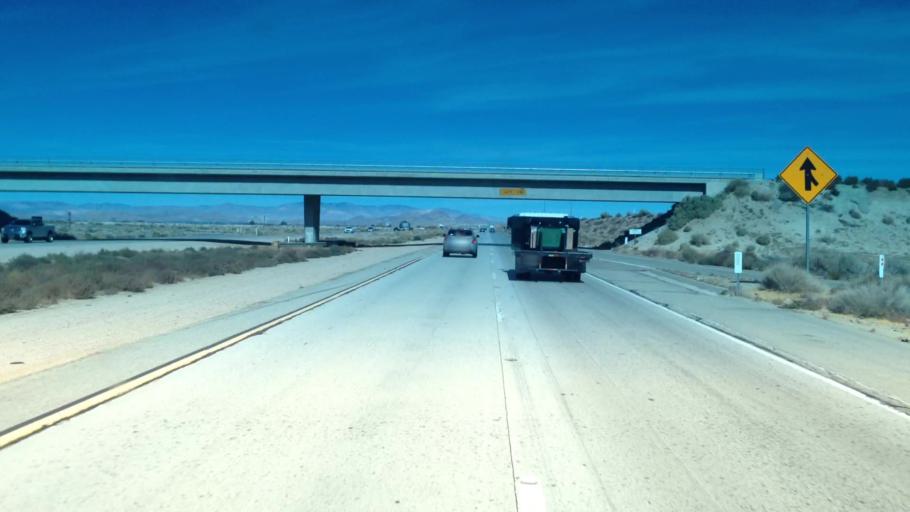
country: US
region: California
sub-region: Los Angeles County
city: Lancaster
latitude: 34.7469
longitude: -118.1702
